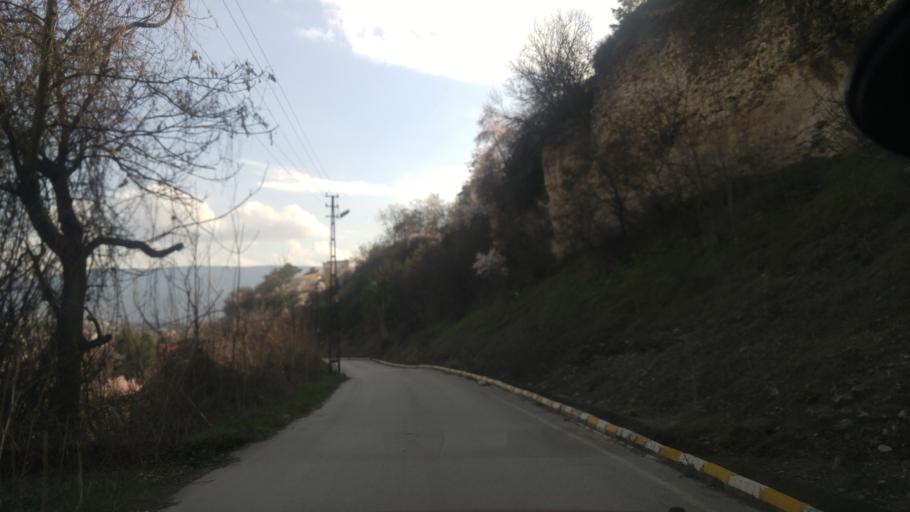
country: TR
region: Karabuk
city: Safranbolu
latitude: 41.2553
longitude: 32.6839
